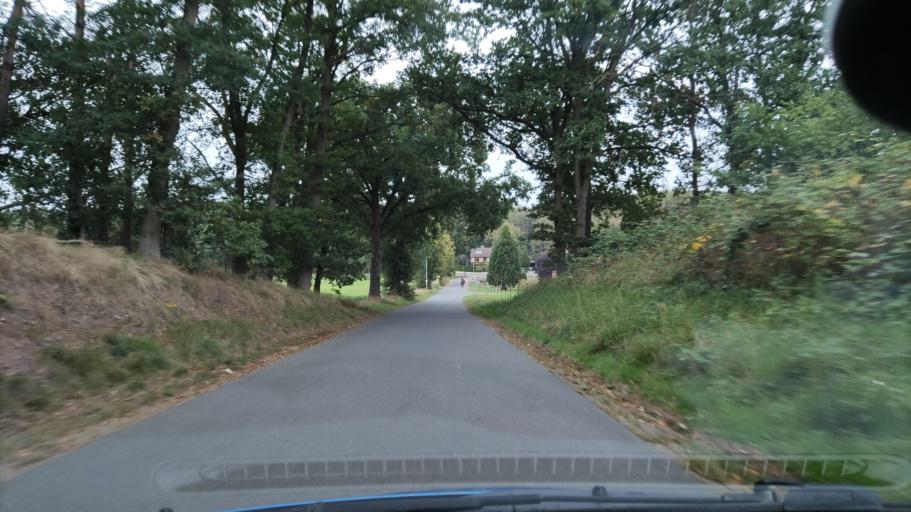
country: DE
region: Lower Saxony
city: Karwitz
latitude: 53.0913
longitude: 11.0022
